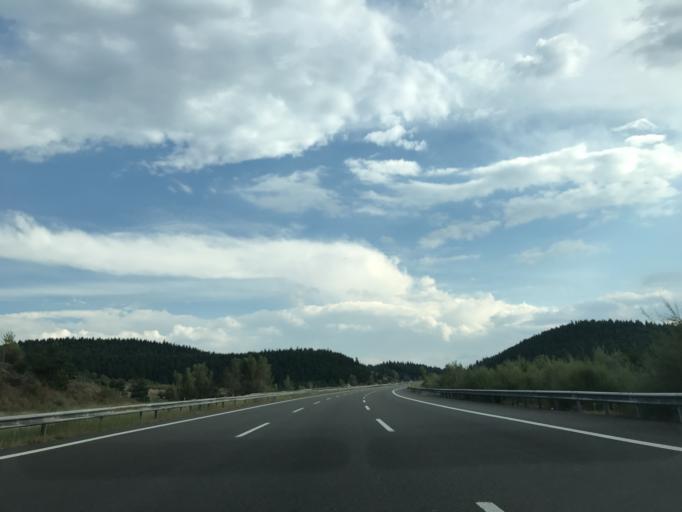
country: TR
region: Bolu
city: Gerede
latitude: 40.6314
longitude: 32.2380
